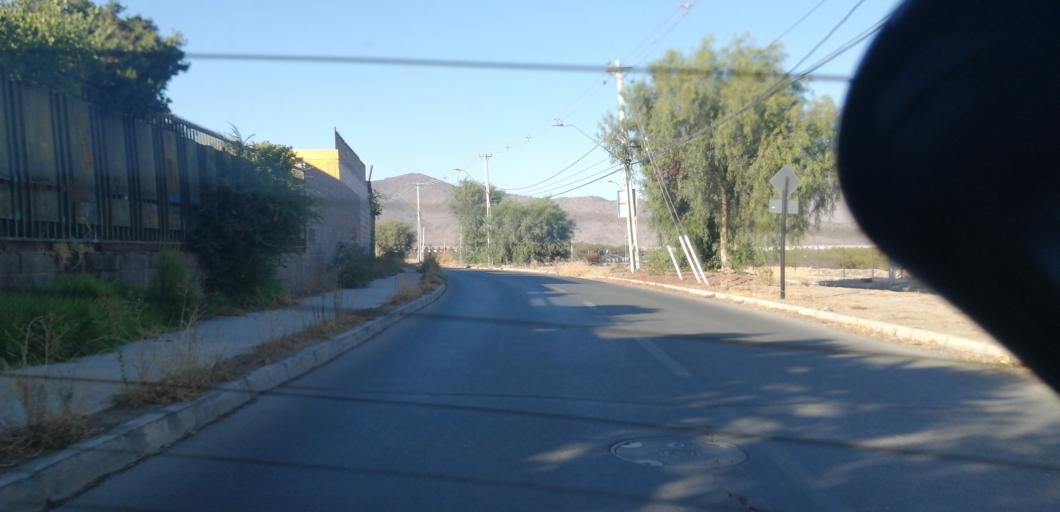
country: CL
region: Santiago Metropolitan
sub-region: Provincia de Santiago
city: Lo Prado
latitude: -33.4565
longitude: -70.8554
